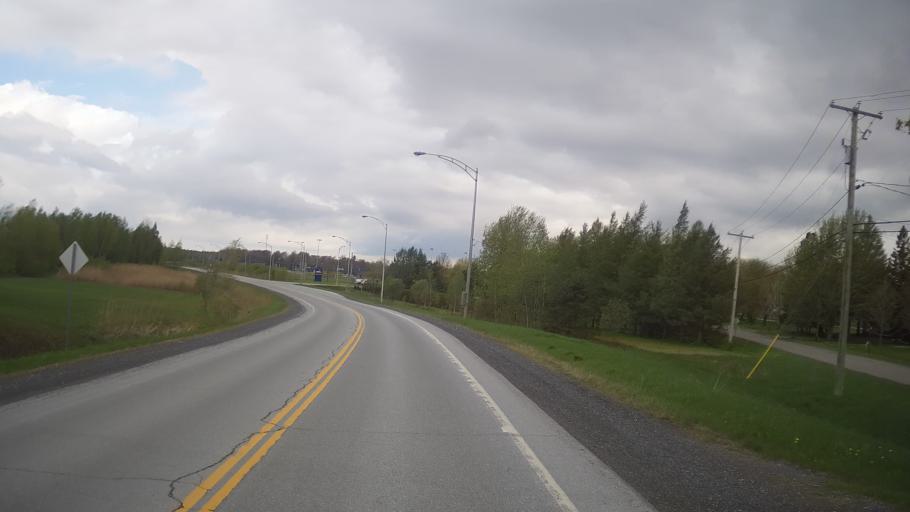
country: CA
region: Quebec
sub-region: Monteregie
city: Farnham
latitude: 45.2708
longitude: -72.9509
